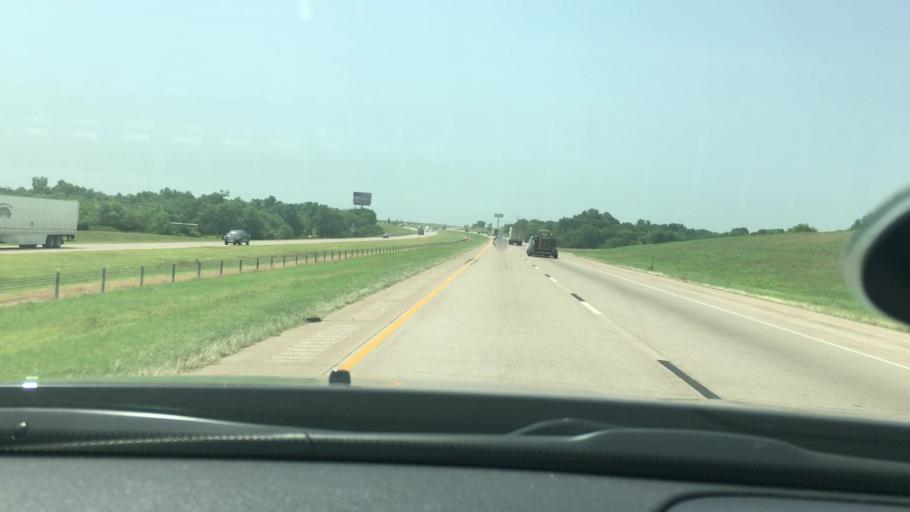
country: US
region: Oklahoma
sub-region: Garvin County
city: Pauls Valley
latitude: 34.7183
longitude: -97.2517
